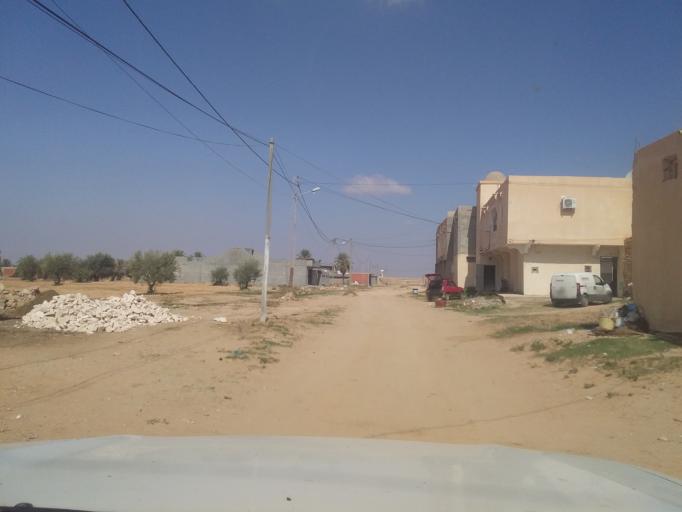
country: TN
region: Qabis
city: Matmata
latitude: 33.6201
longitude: 10.2695
